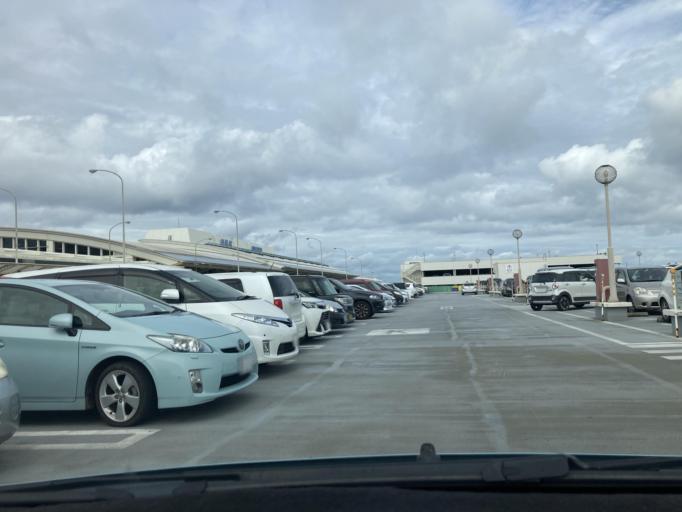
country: JP
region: Okinawa
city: Naha-shi
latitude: 26.2070
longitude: 127.6516
